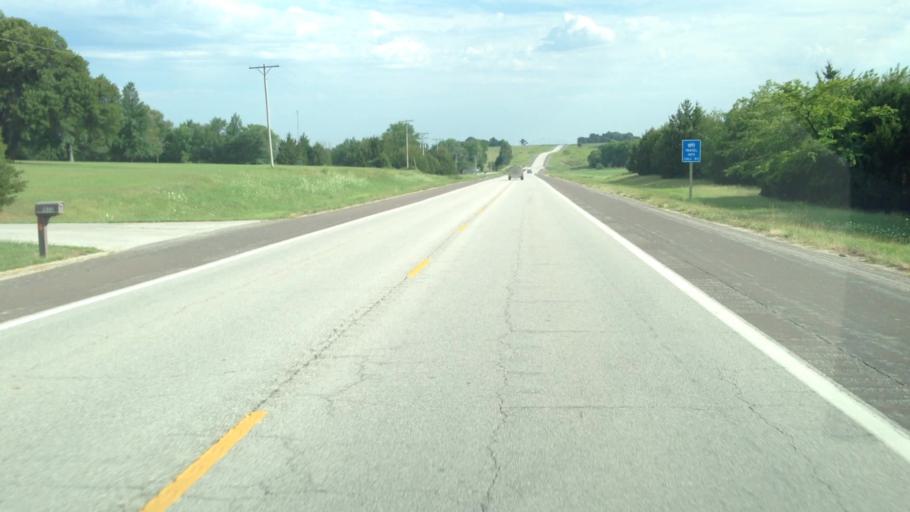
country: US
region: Kansas
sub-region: Woodson County
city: Yates Center
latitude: 37.8696
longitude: -95.7387
